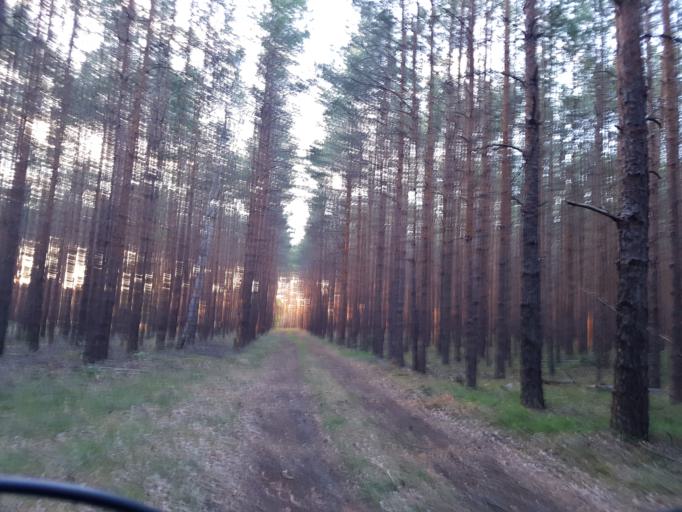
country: DE
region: Brandenburg
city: Trobitz
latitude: 51.5985
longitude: 13.4100
